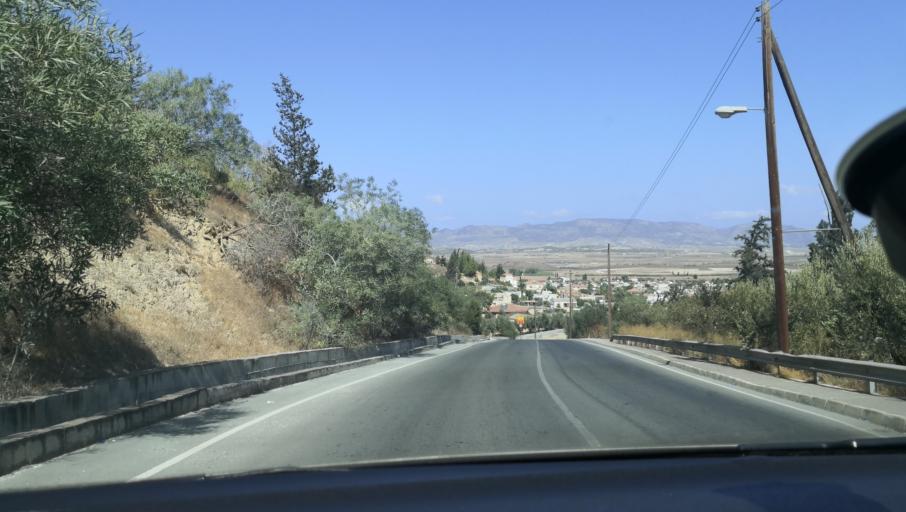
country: CY
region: Lefkosia
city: Mammari
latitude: 35.1708
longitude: 33.2018
